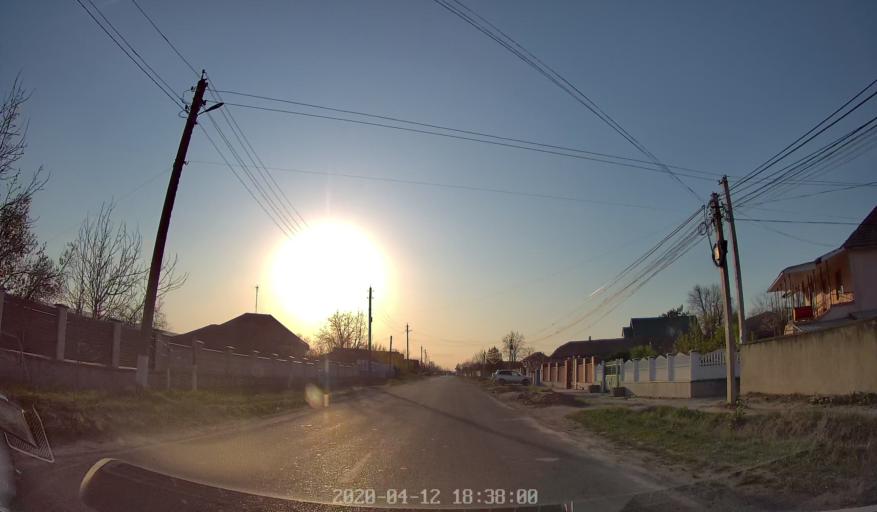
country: MD
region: Chisinau
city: Vadul lui Voda
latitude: 47.1231
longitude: 29.0067
